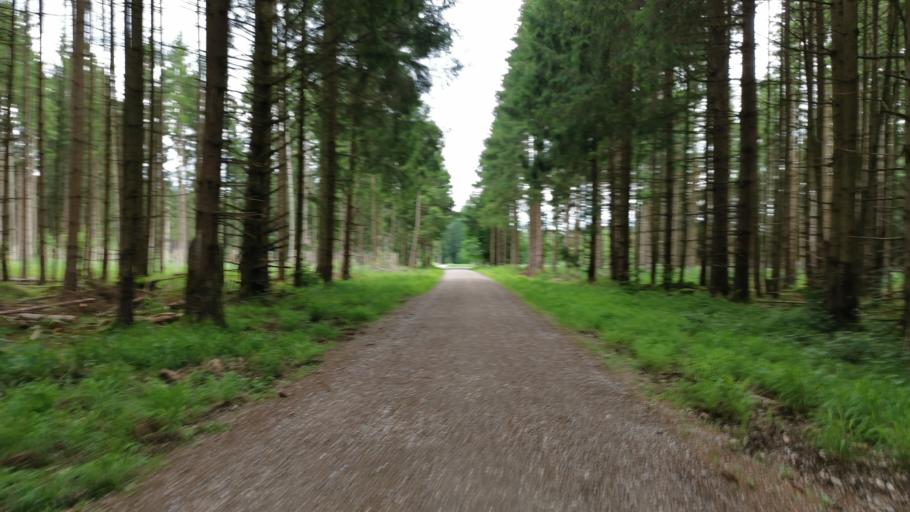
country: DE
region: Bavaria
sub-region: Upper Bavaria
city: Baierbrunn
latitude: 48.0483
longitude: 11.4904
